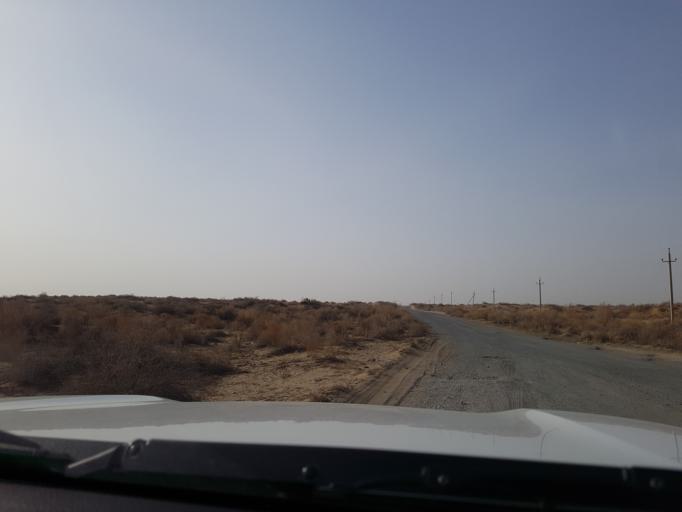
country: UZ
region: Xorazm
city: Hazorasp
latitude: 41.1871
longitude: 61.0315
